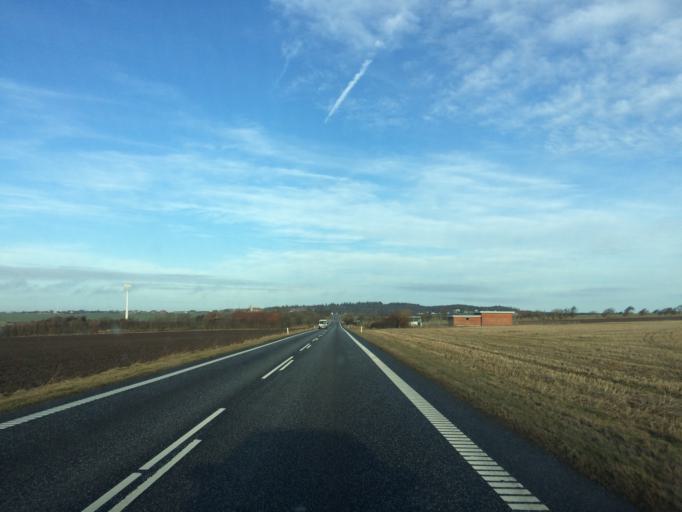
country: DK
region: North Denmark
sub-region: Thisted Kommune
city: Hurup
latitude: 56.6962
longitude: 8.4047
